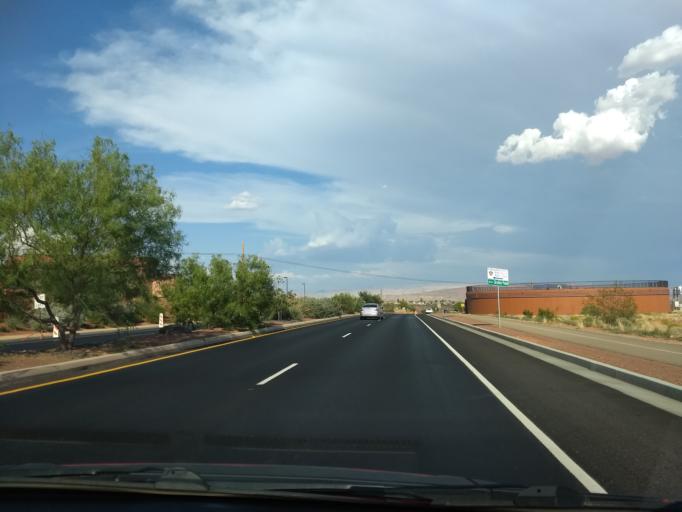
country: US
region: Utah
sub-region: Washington County
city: Saint George
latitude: 37.1132
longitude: -113.5740
